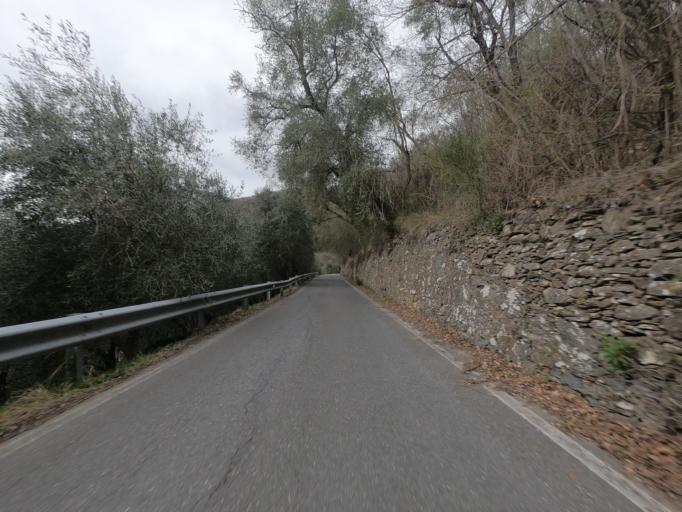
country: IT
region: Liguria
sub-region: Provincia di Savona
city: Testico
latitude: 44.0270
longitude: 8.0127
